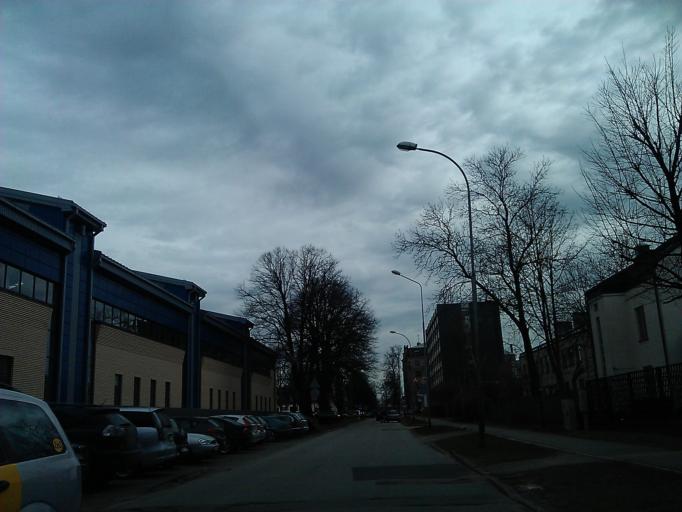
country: LV
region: Riga
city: Riga
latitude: 56.9717
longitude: 24.1495
